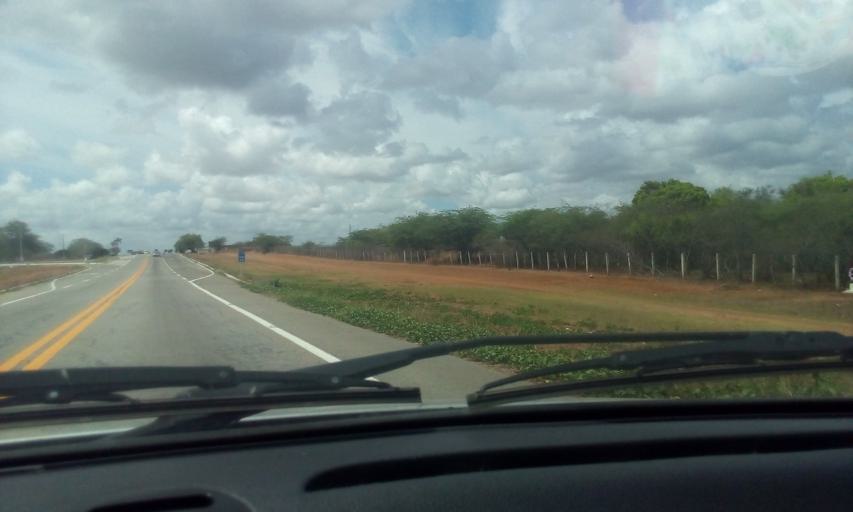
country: BR
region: Rio Grande do Norte
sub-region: Tangara
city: Tangara
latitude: -6.1020
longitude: -35.7033
